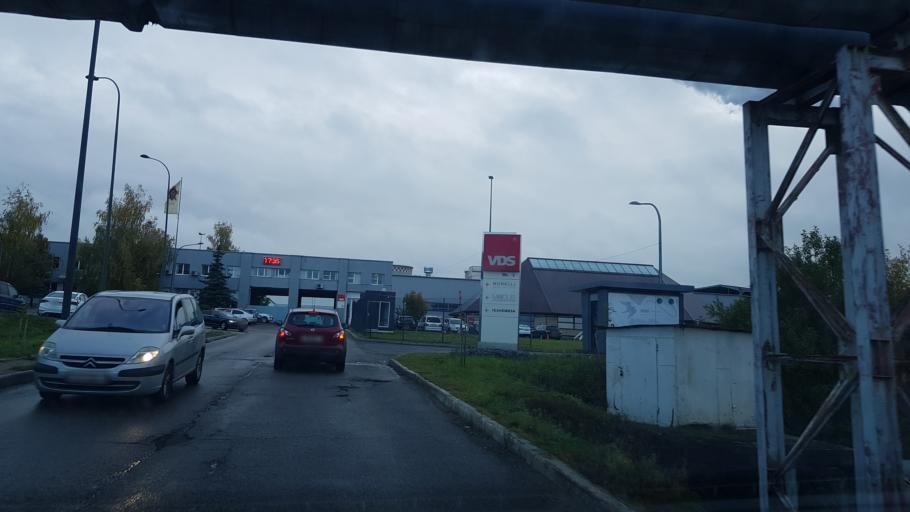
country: BY
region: Minsk
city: Malinovka
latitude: 53.8771
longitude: 27.4100
